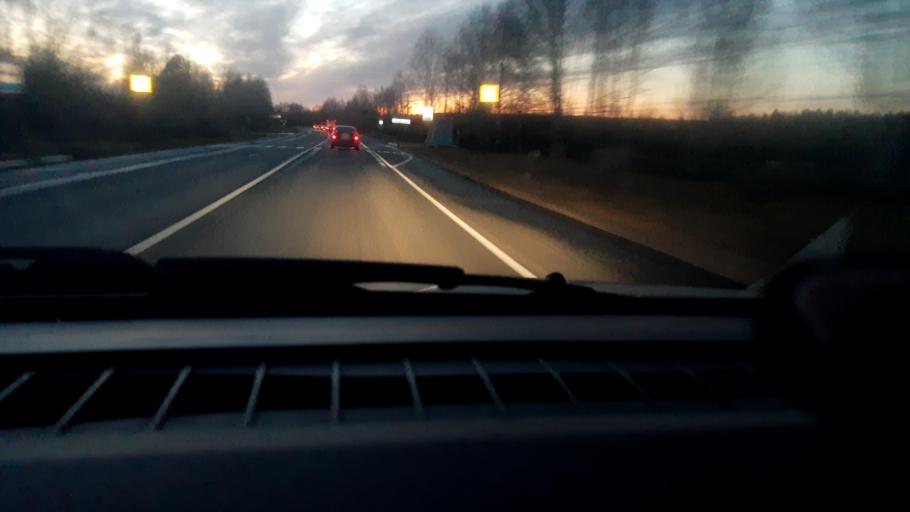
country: RU
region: Nizjnij Novgorod
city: Sukhobezvodnoye
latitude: 56.8611
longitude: 44.8547
